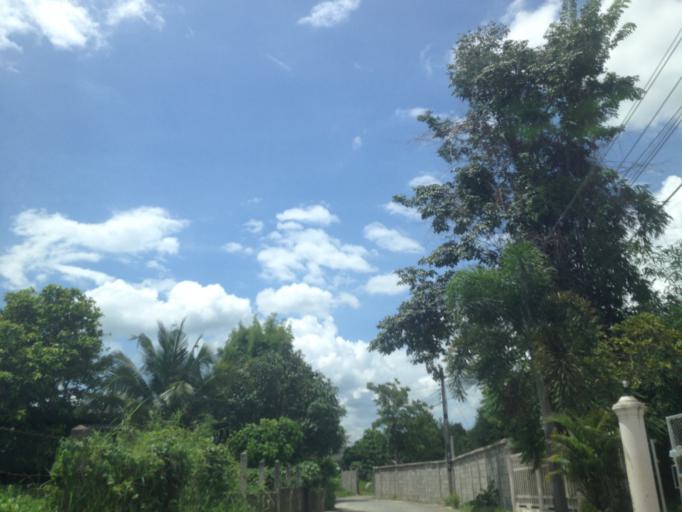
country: TH
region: Chiang Mai
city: Hang Dong
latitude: 18.6895
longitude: 98.8927
